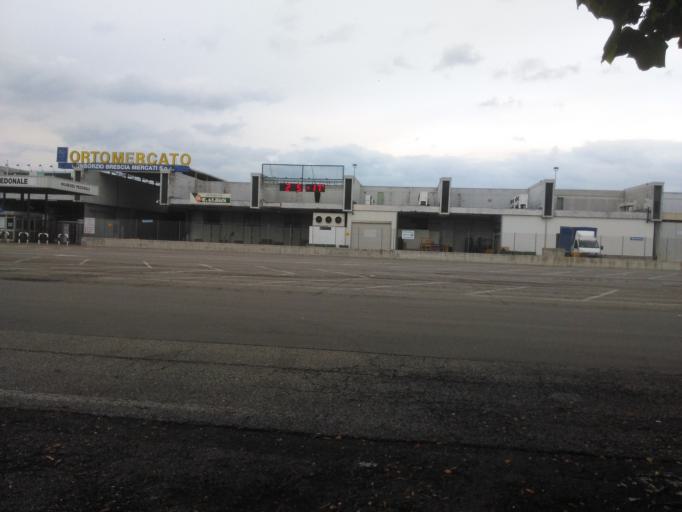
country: IT
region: Lombardy
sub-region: Provincia di Brescia
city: Roncadelle
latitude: 45.5326
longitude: 10.1761
